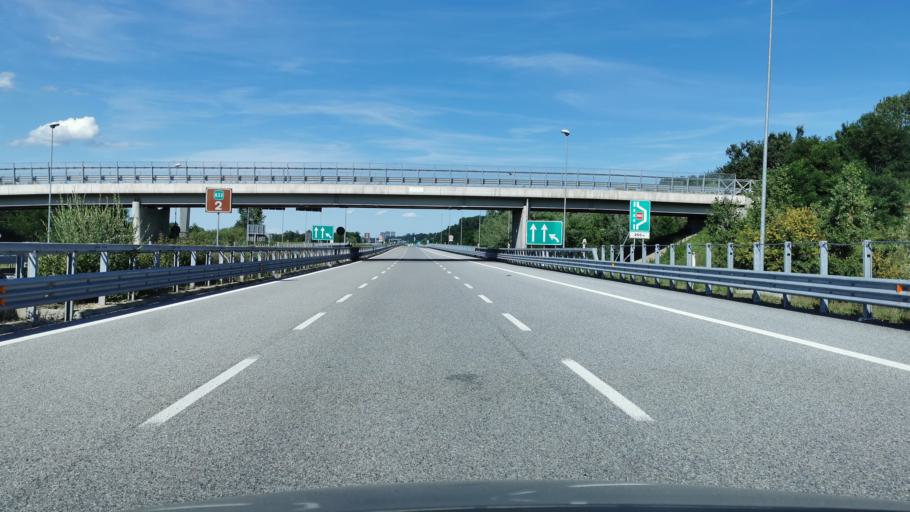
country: IT
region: Piedmont
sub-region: Provincia di Cuneo
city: Castelletto Stura
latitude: 44.4322
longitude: 7.6115
